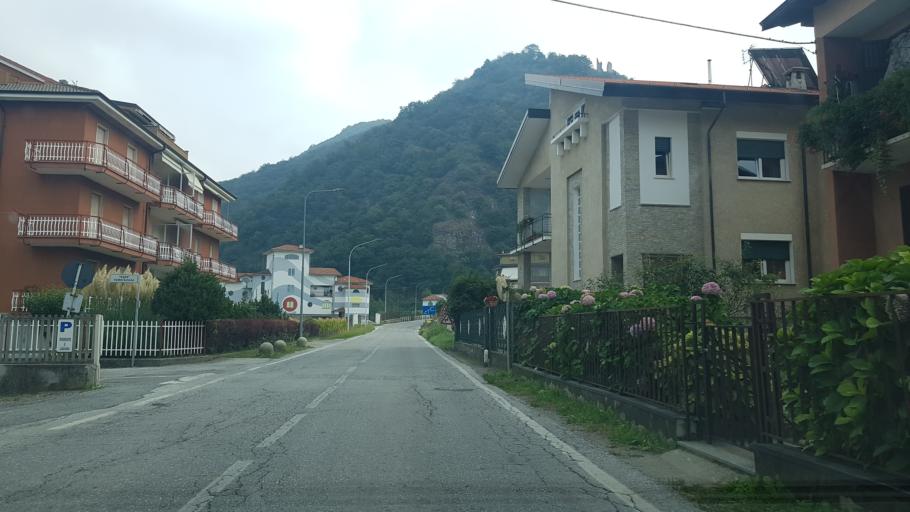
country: IT
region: Piedmont
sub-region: Provincia di Cuneo
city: Chiusa di Pesio
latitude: 44.3272
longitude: 7.6774
